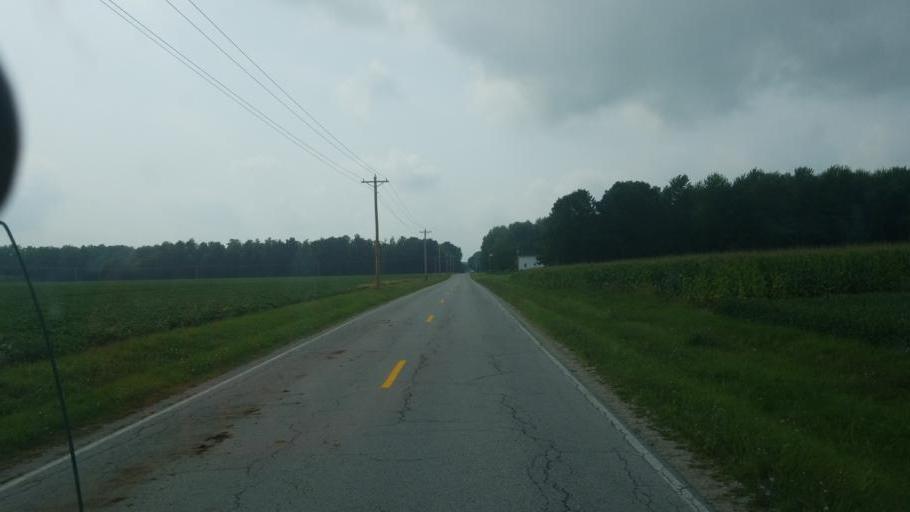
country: US
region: Ohio
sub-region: Huron County
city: Greenwich
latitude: 41.0520
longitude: -82.5306
